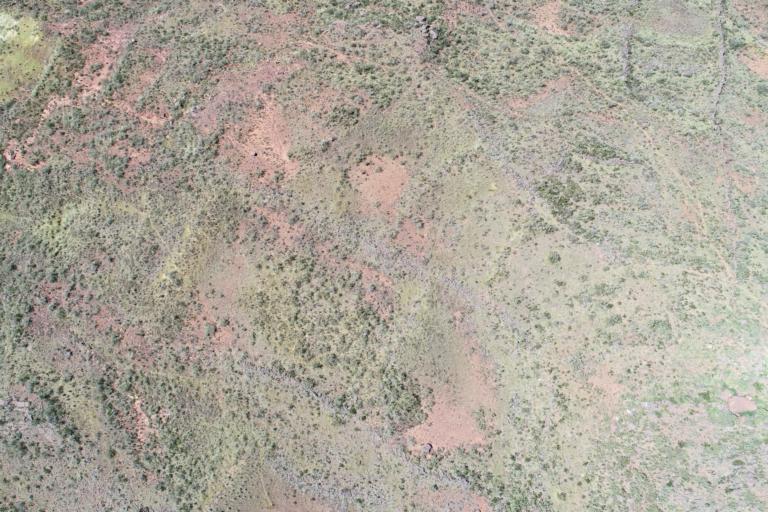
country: BO
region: La Paz
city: Tiahuanaco
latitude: -16.6055
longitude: -68.7744
